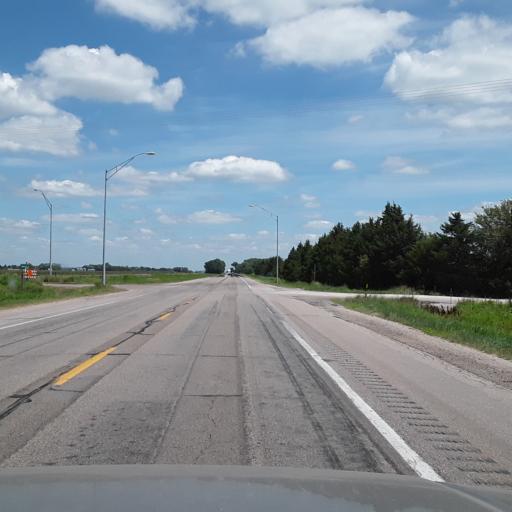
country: US
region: Nebraska
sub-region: Nance County
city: Genoa
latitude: 41.3432
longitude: -97.5992
